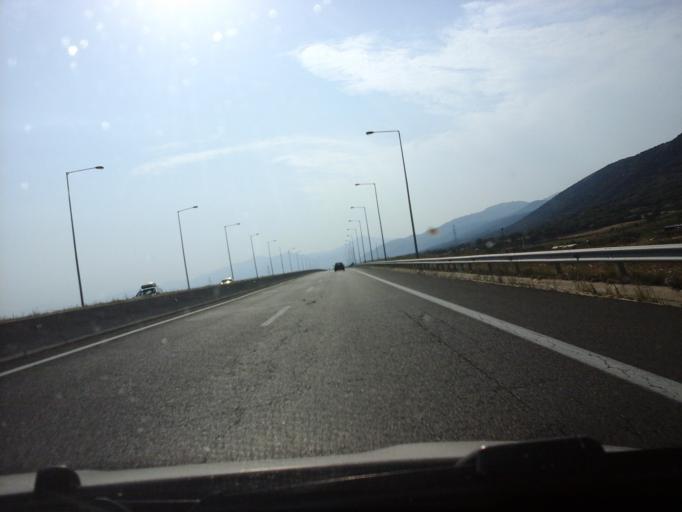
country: GR
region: East Macedonia and Thrace
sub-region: Nomos Rodopis
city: Iasmos
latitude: 41.1154
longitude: 25.1169
